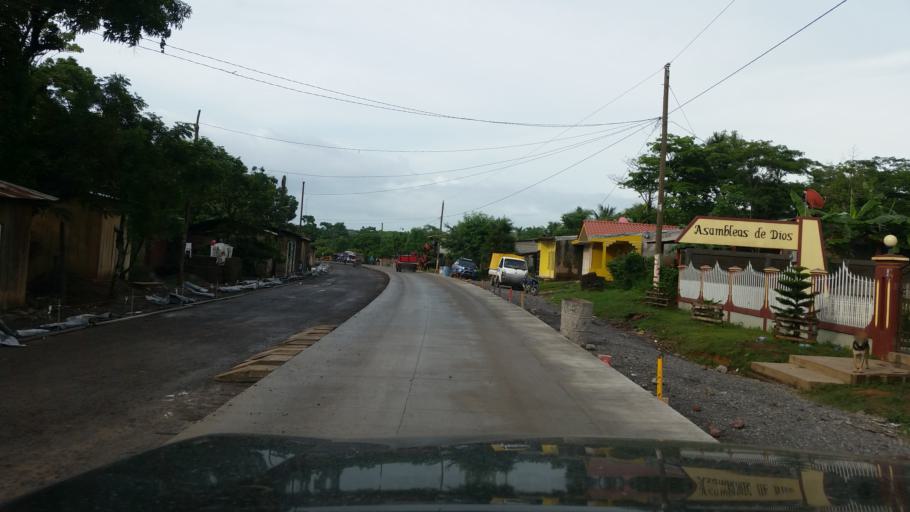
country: NI
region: Matagalpa
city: Rio Blanco
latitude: 13.0727
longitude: -85.0632
